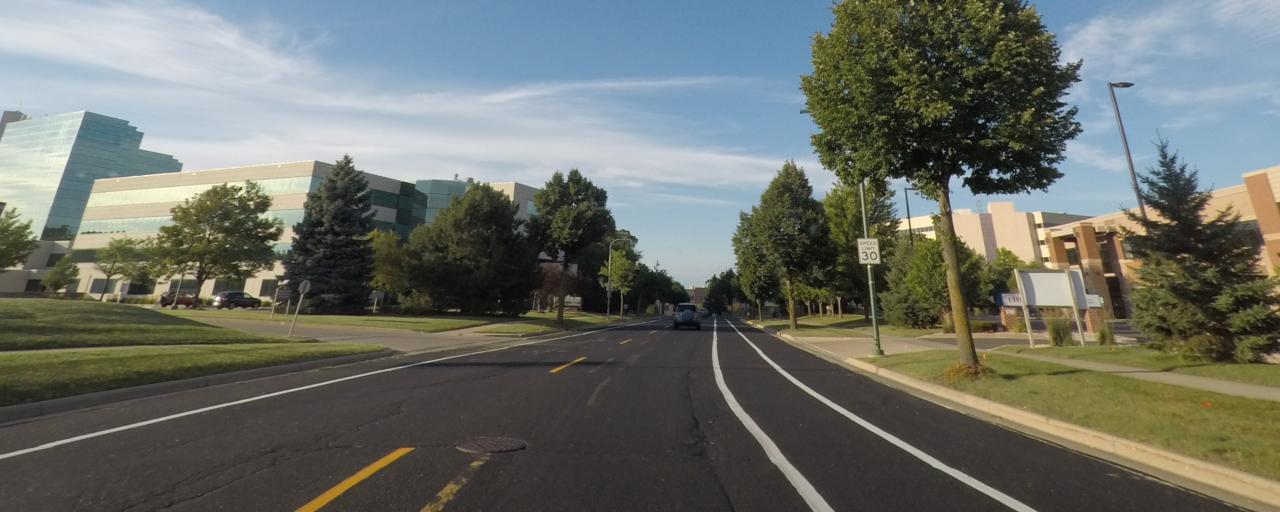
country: US
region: Wisconsin
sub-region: Dane County
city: Middleton
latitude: 43.0875
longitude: -89.5282
